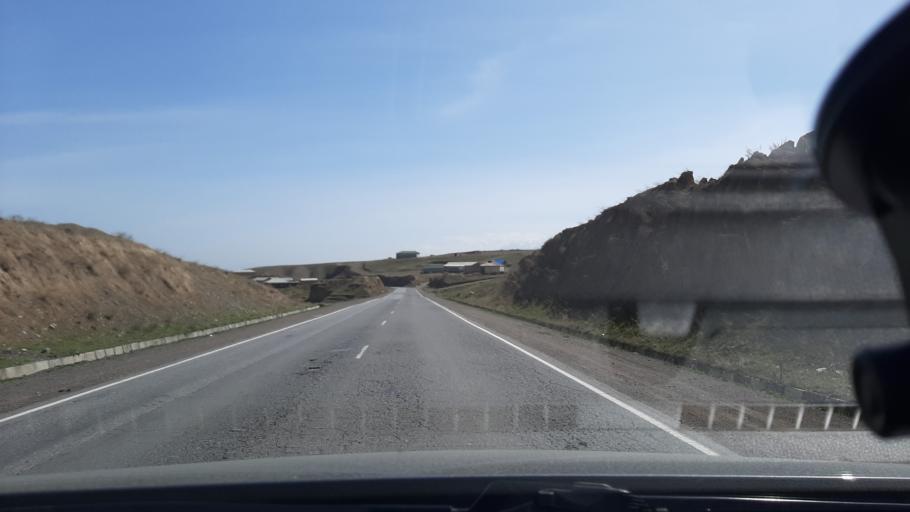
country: TJ
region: Viloyati Sughd
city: Shahriston
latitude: 39.7625
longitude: 68.8086
